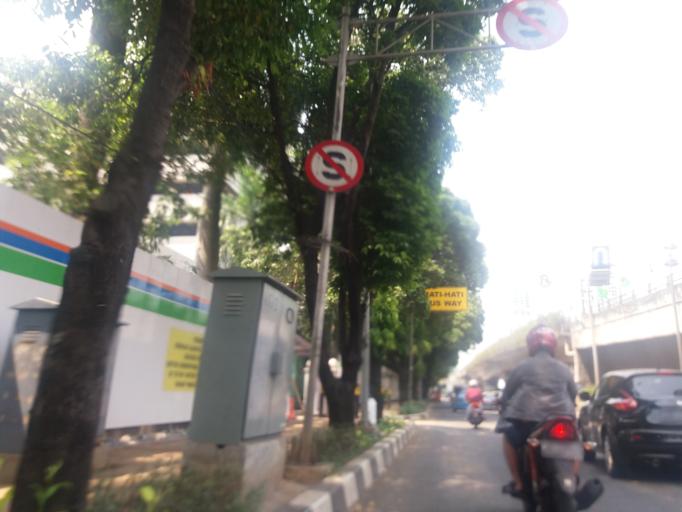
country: ID
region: Jakarta Raya
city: Jakarta
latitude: -6.2356
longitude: 106.8260
